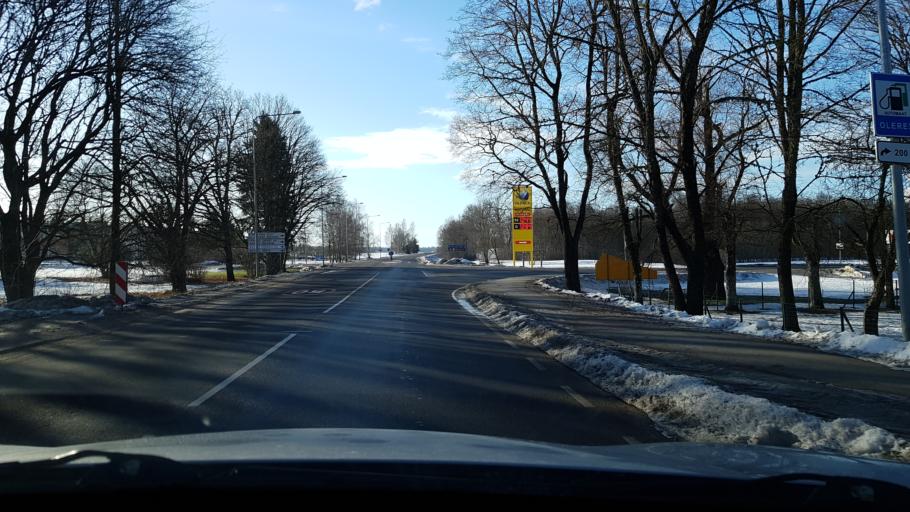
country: EE
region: Jogevamaa
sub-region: Poltsamaa linn
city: Poltsamaa
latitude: 58.7332
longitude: 25.7669
